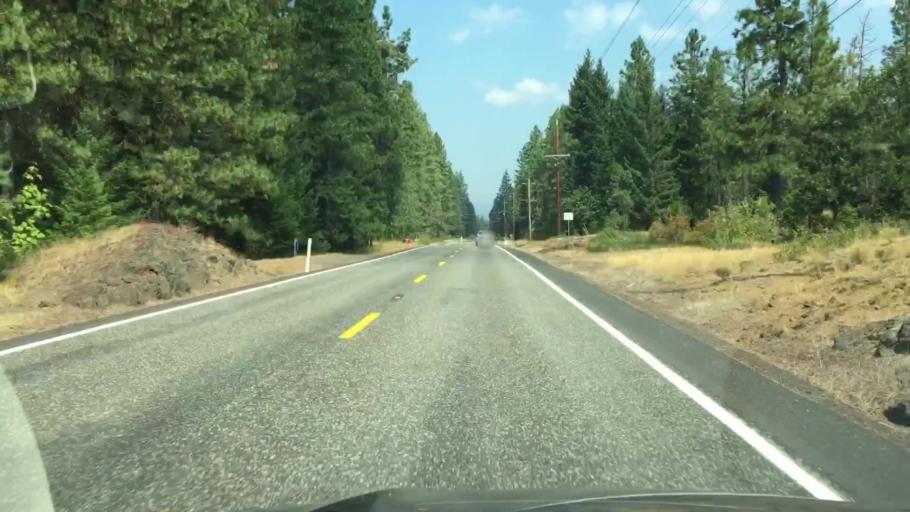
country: US
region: Washington
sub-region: Klickitat County
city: White Salmon
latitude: 45.9304
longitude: -121.4951
